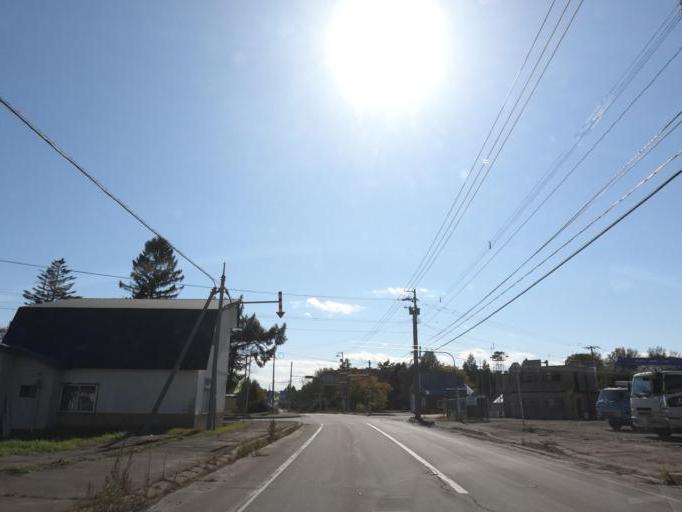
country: JP
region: Hokkaido
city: Obihiro
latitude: 42.6754
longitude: 143.3111
